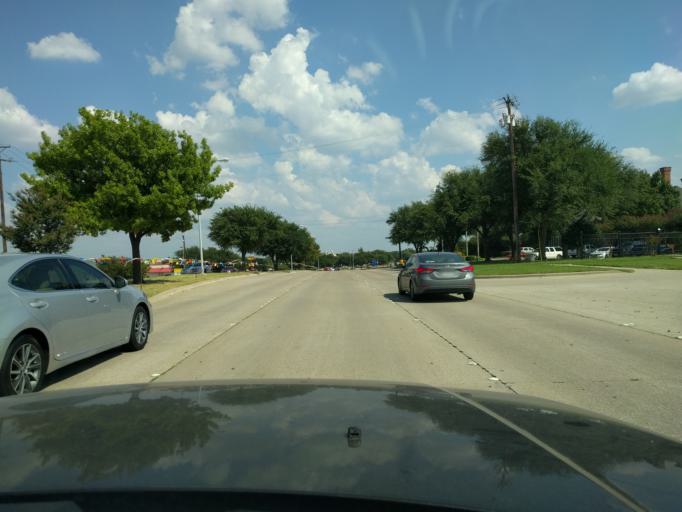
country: US
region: Texas
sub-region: Collin County
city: Plano
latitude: 33.0570
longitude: -96.6886
